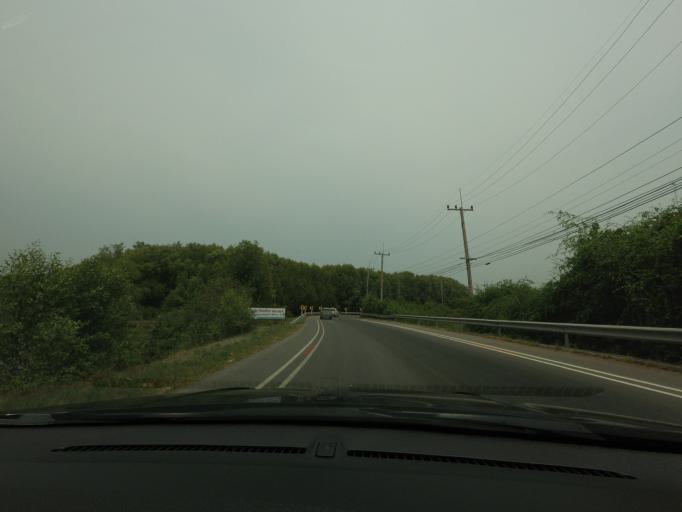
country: TH
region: Phetchaburi
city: Khao Yoi
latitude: 13.2917
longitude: 99.9175
